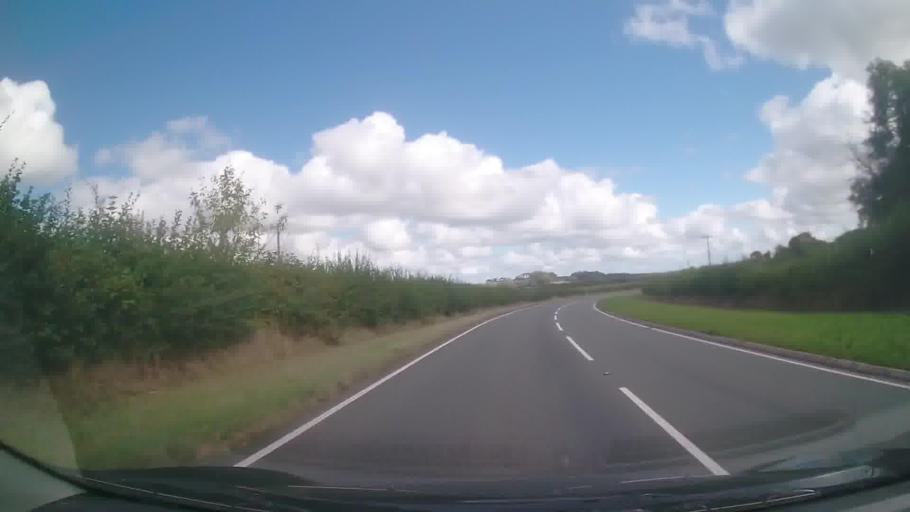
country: GB
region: Wales
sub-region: Pembrokeshire
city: Pembroke
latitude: 51.6855
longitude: -4.8792
